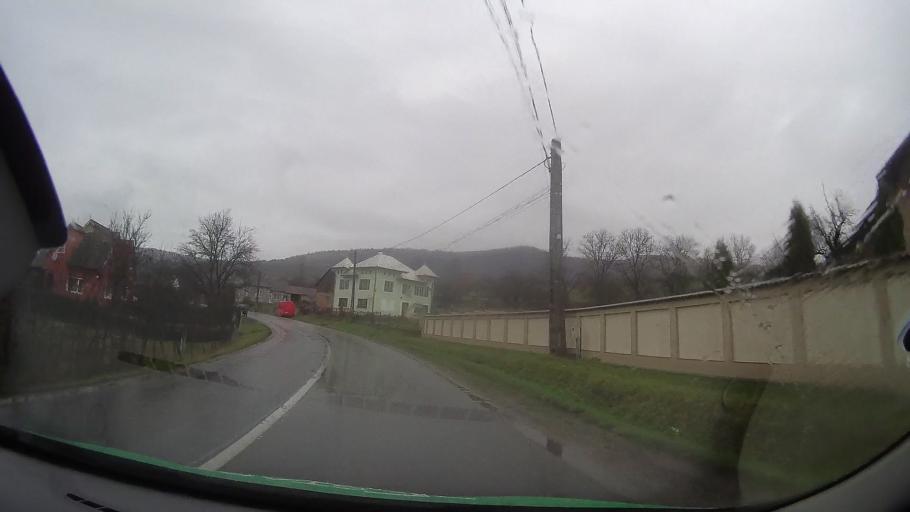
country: RO
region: Bistrita-Nasaud
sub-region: Comuna Mariselu
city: Mariselu
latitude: 47.0141
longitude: 24.5535
